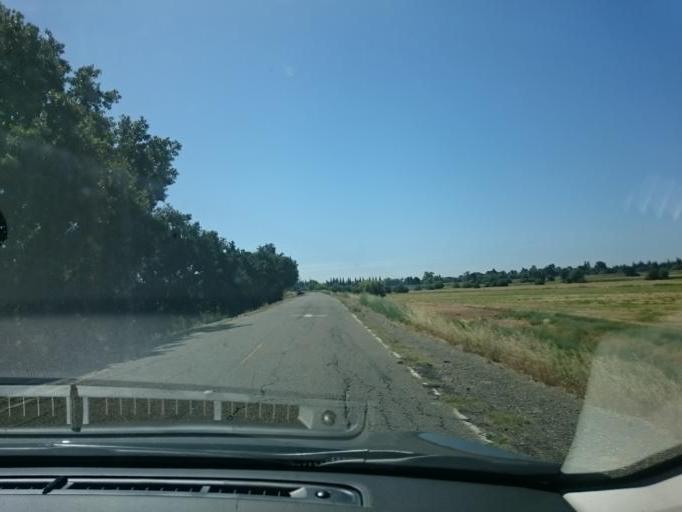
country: US
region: California
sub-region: Yolo County
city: West Sacramento
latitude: 38.5262
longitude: -121.5308
